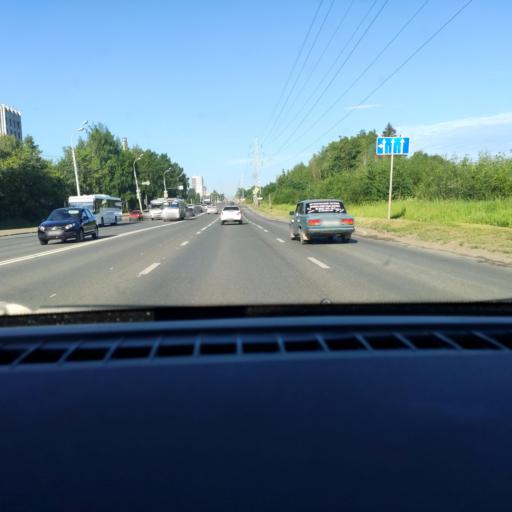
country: RU
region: Udmurtiya
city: Khokhryaki
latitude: 56.8976
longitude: 53.2989
